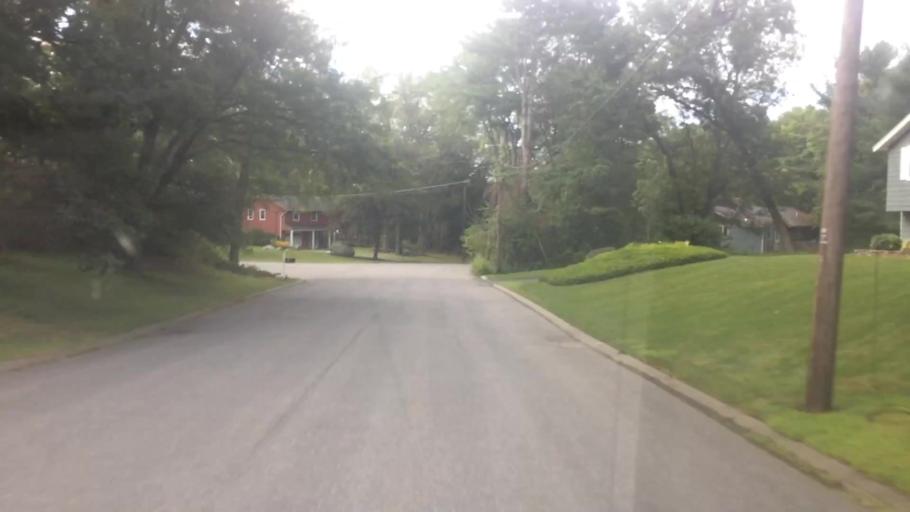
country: US
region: Massachusetts
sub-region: Middlesex County
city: Acton
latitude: 42.4598
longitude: -71.4378
